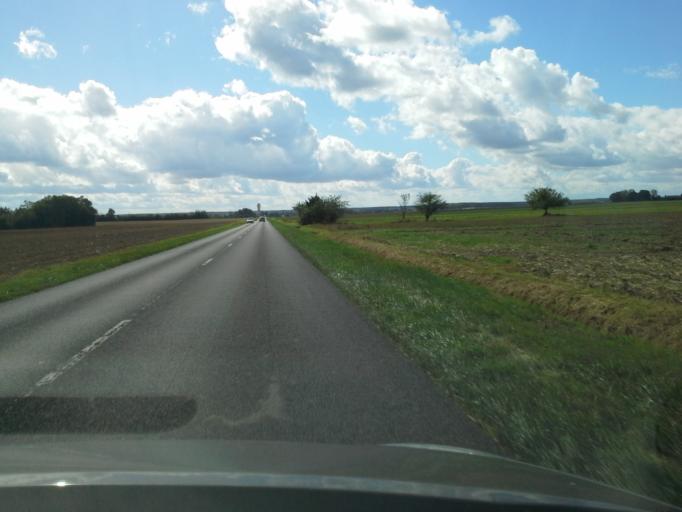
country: FR
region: Centre
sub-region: Departement du Loir-et-Cher
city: Pontlevoy
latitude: 47.4136
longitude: 1.2738
